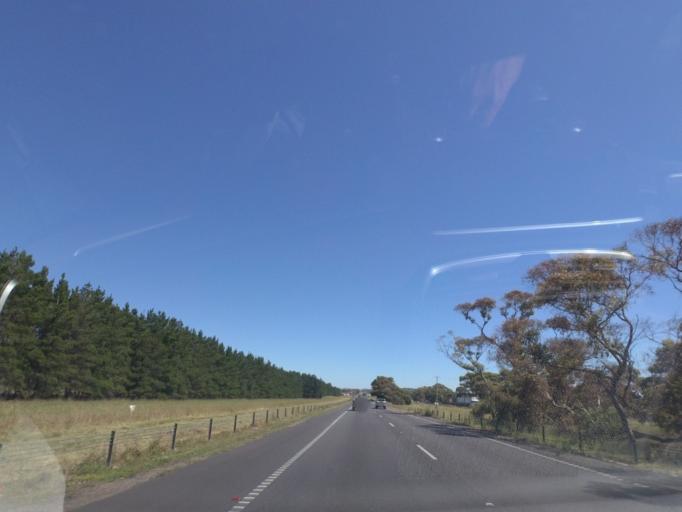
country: AU
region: Victoria
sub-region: Hume
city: Craigieburn
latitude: -37.5189
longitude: 144.9491
